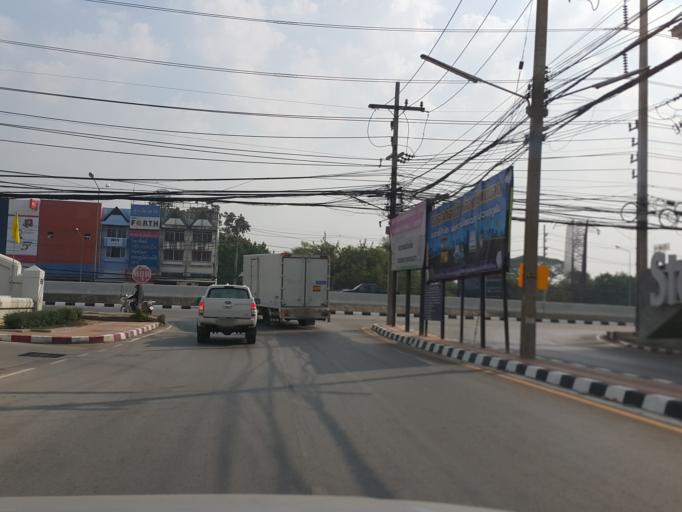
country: TH
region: Chiang Mai
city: Chiang Mai
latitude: 18.8008
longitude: 99.0189
